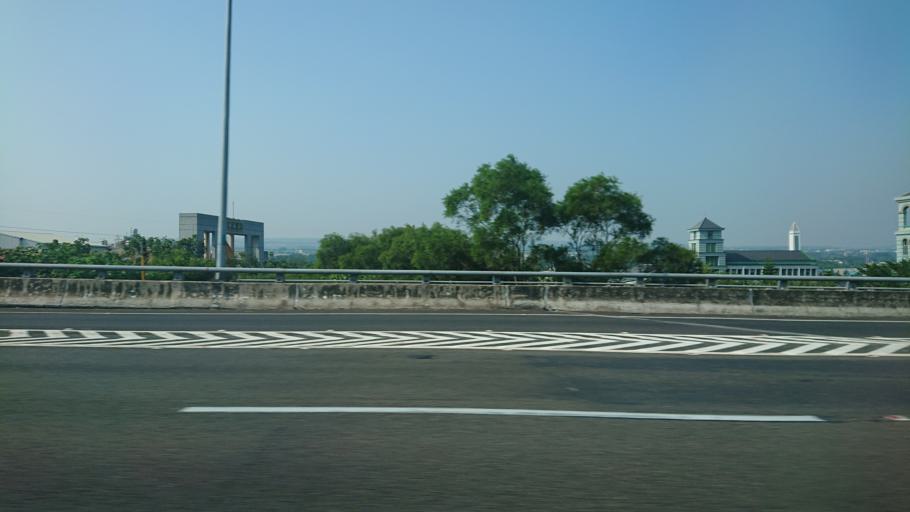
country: TW
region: Taiwan
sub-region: Nantou
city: Nantou
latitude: 23.8479
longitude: 120.7040
